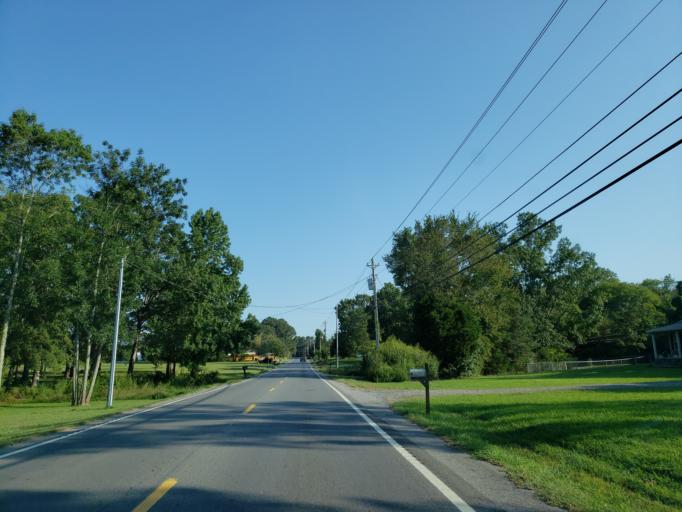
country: US
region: Tennessee
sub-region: Bradley County
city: Wildwood Lake
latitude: 35.0857
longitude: -84.8216
